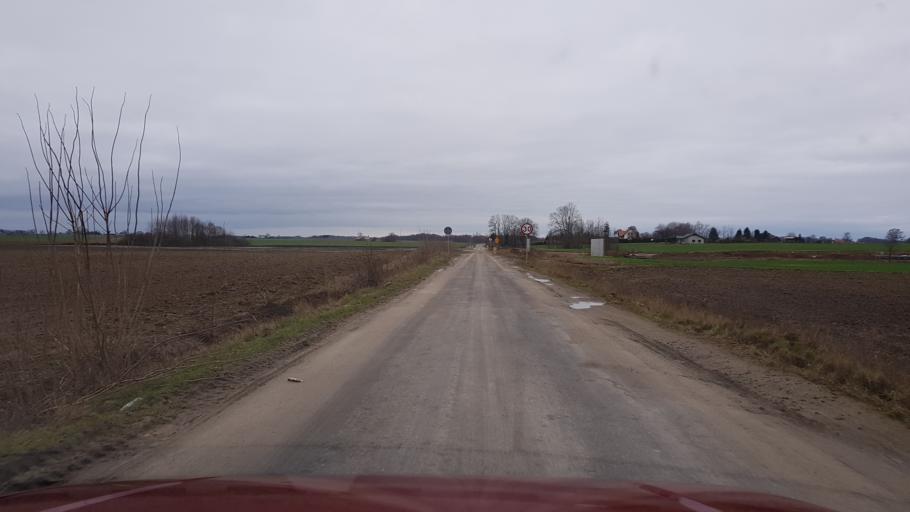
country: PL
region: West Pomeranian Voivodeship
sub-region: Powiat koszalinski
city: Mielno
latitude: 54.1918
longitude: 16.0494
